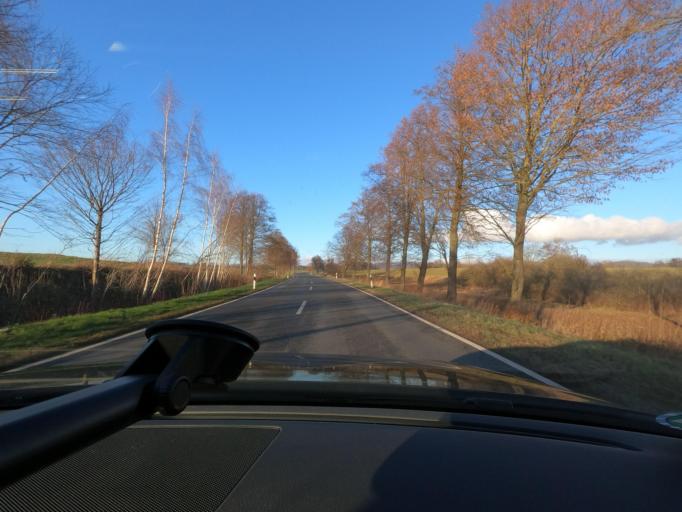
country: DE
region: Lower Saxony
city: Herzberg am Harz
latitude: 51.6342
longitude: 10.3302
